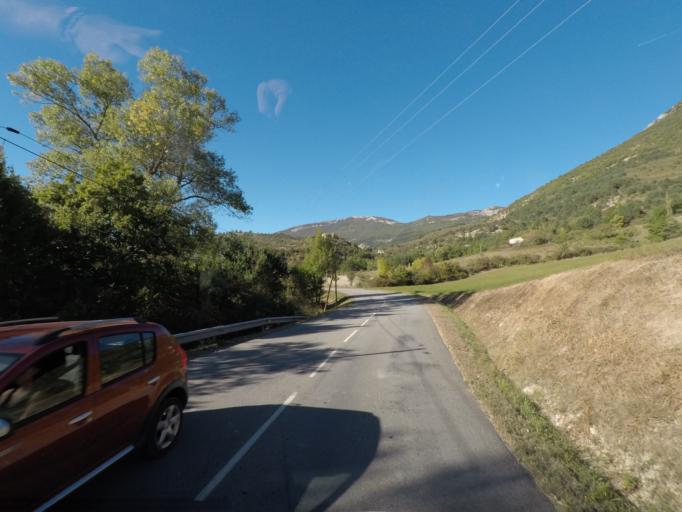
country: FR
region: Rhone-Alpes
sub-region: Departement de la Drome
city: Buis-les-Baronnies
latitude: 44.4691
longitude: 5.4207
